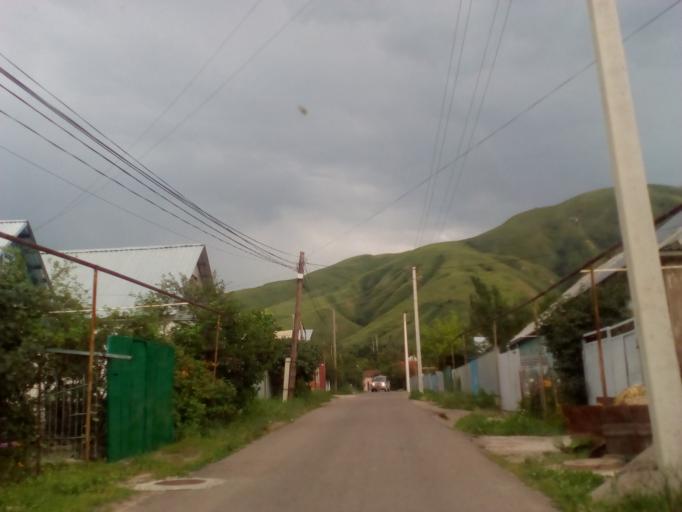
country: KZ
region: Almaty Oblysy
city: Burunday
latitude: 43.1589
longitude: 76.4093
